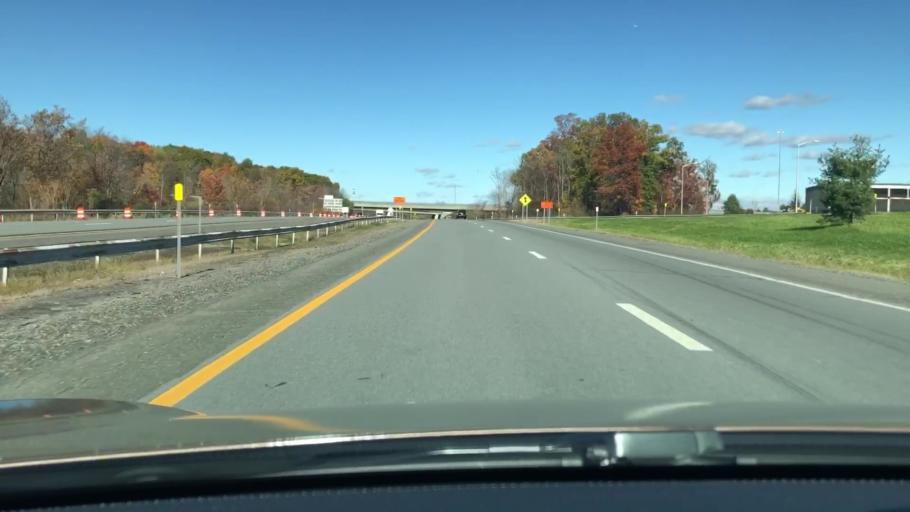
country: US
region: New York
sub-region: Orange County
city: Gardnertown
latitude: 41.5107
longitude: -74.0741
